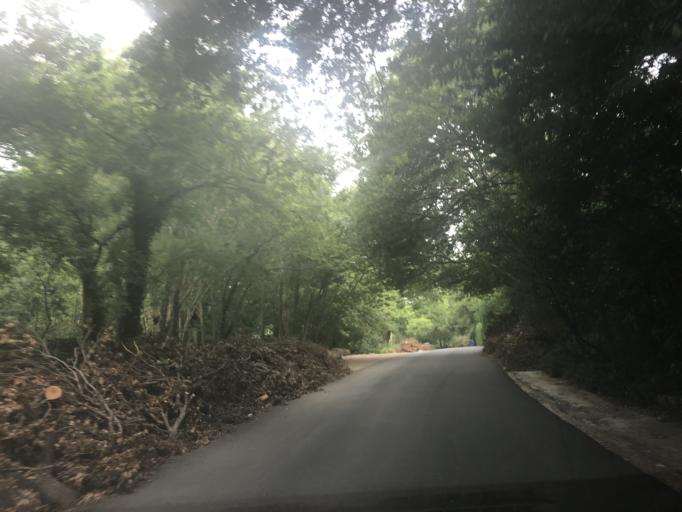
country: US
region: Texas
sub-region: Dallas County
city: University Park
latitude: 32.8585
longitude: -96.8297
